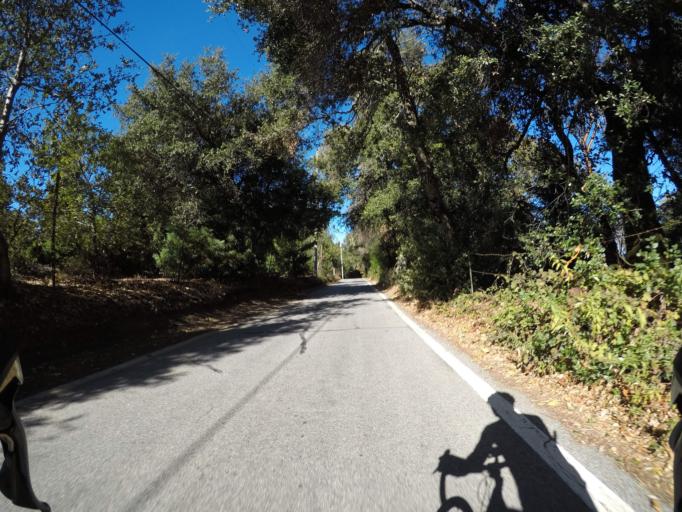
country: US
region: California
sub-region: Santa Clara County
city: Lexington Hills
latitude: 37.1552
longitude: -122.0004
